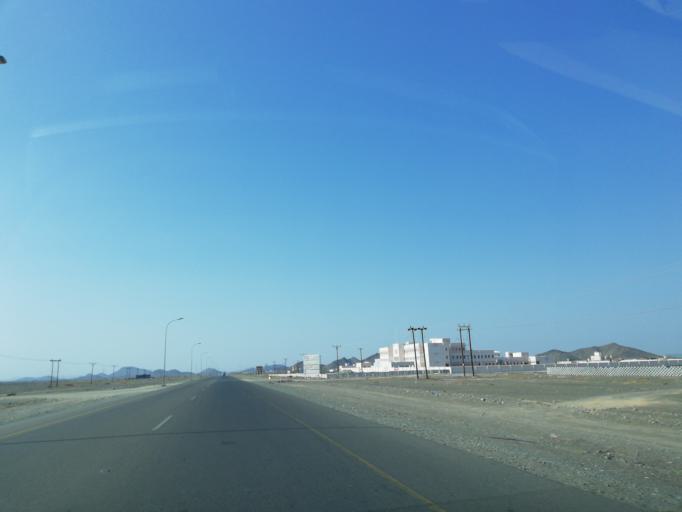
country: OM
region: Ash Sharqiyah
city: Ibra'
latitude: 22.7688
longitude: 58.1443
